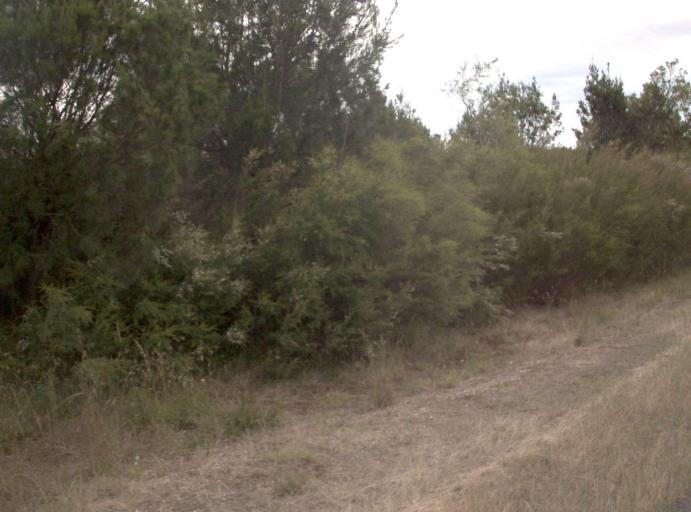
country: AU
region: Victoria
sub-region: East Gippsland
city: Bairnsdale
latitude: -37.9910
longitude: 147.3958
